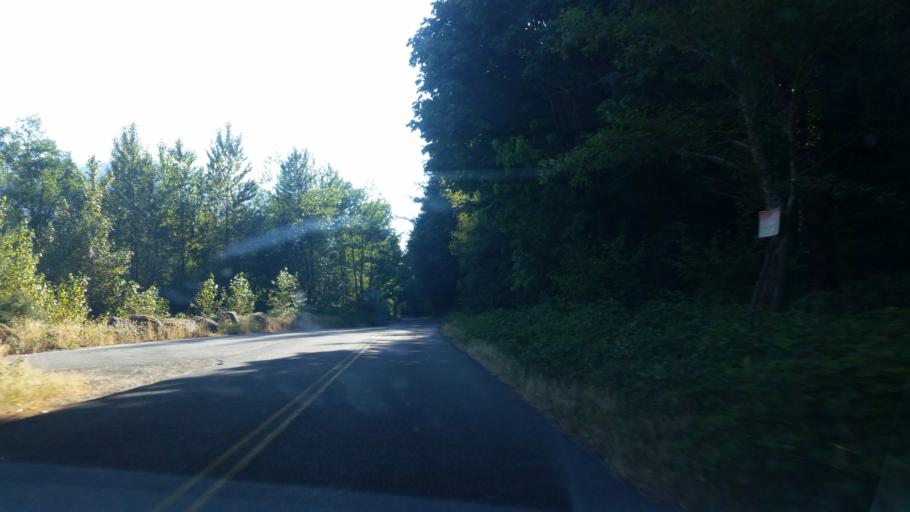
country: US
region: Washington
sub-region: Snohomish County
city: Gold Bar
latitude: 47.8427
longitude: -121.6346
